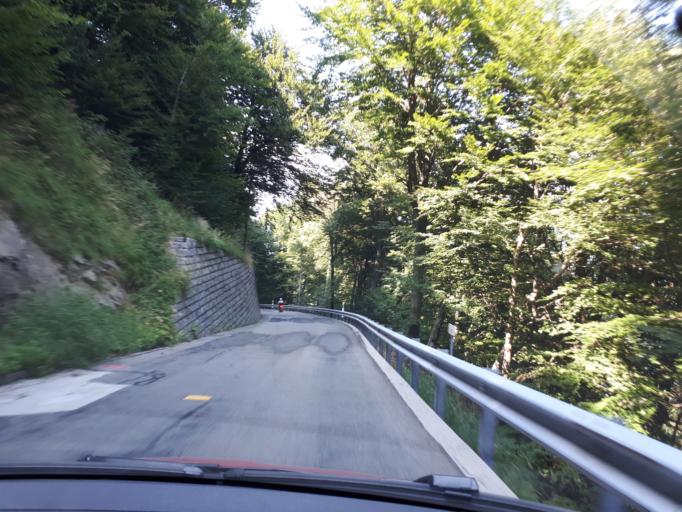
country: CH
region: Ticino
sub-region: Locarno District
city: Magadino
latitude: 46.1168
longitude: 8.8480
